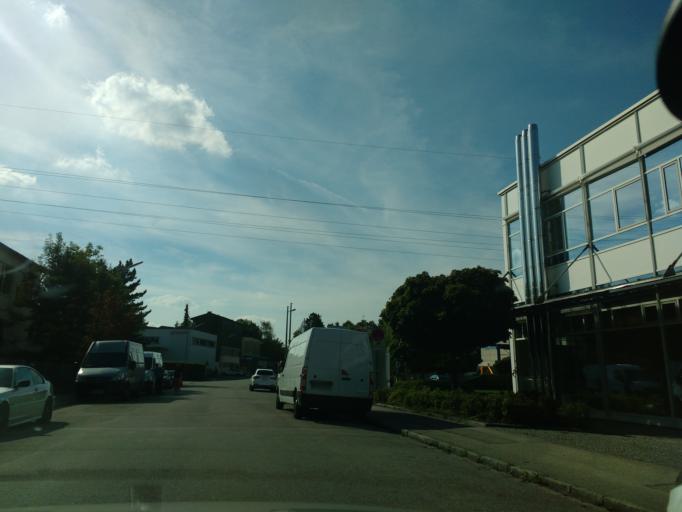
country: DE
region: Bavaria
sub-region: Upper Bavaria
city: Grafelfing
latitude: 48.1222
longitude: 11.4494
